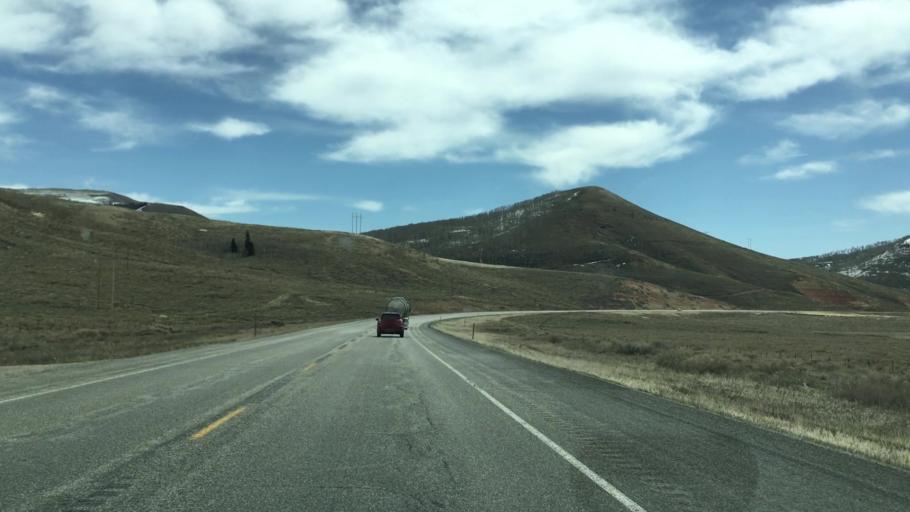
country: US
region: Utah
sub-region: Wasatch County
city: Heber
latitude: 40.2256
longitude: -111.1103
